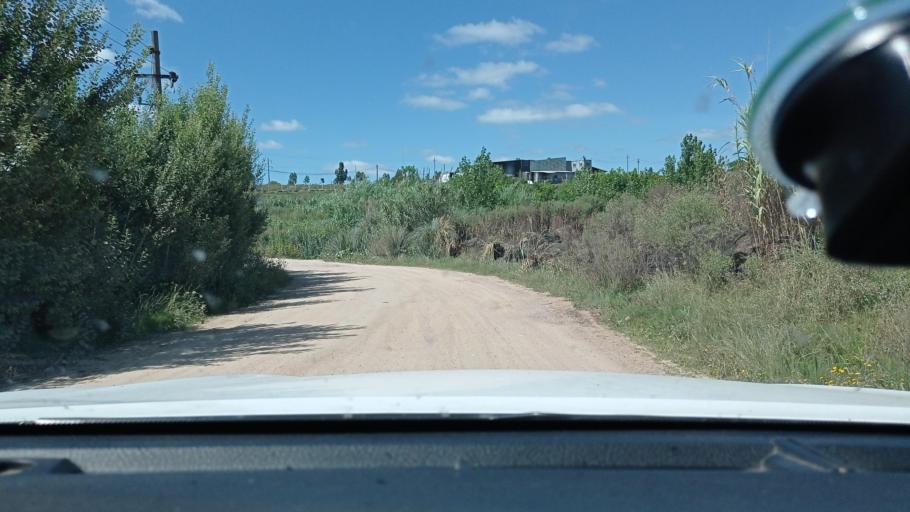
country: UY
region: Canelones
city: Pando
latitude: -34.7248
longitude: -55.9738
